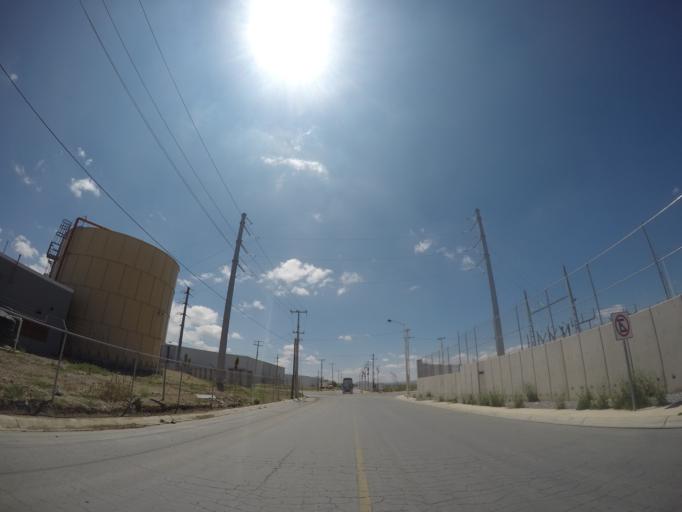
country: MX
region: San Luis Potosi
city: La Pila
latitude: 21.9734
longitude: -100.8772
